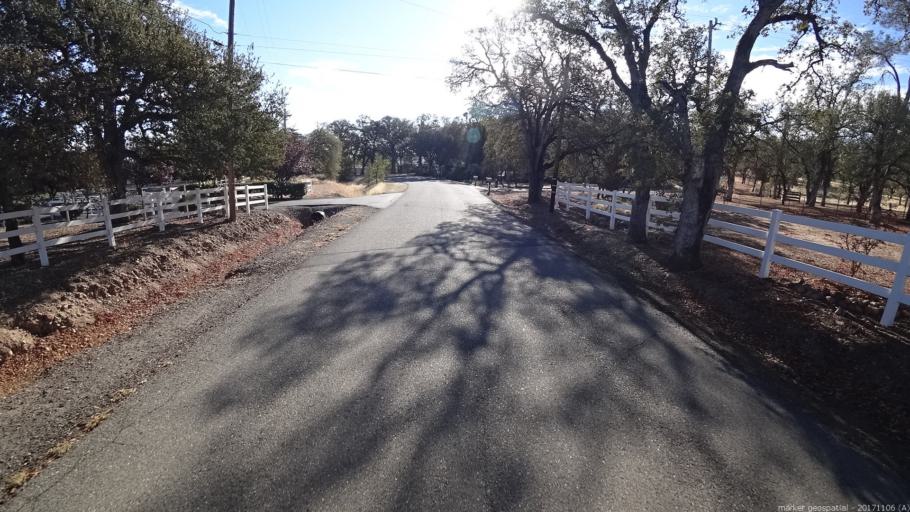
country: US
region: California
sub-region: Shasta County
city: Palo Cedro
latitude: 40.5241
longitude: -122.2434
